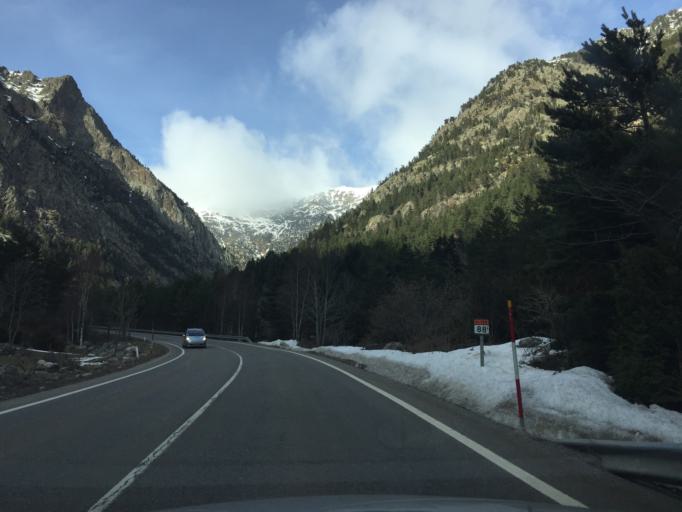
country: ES
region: Aragon
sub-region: Provincia de Huesca
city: Bielsa
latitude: 42.6984
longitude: 0.2027
